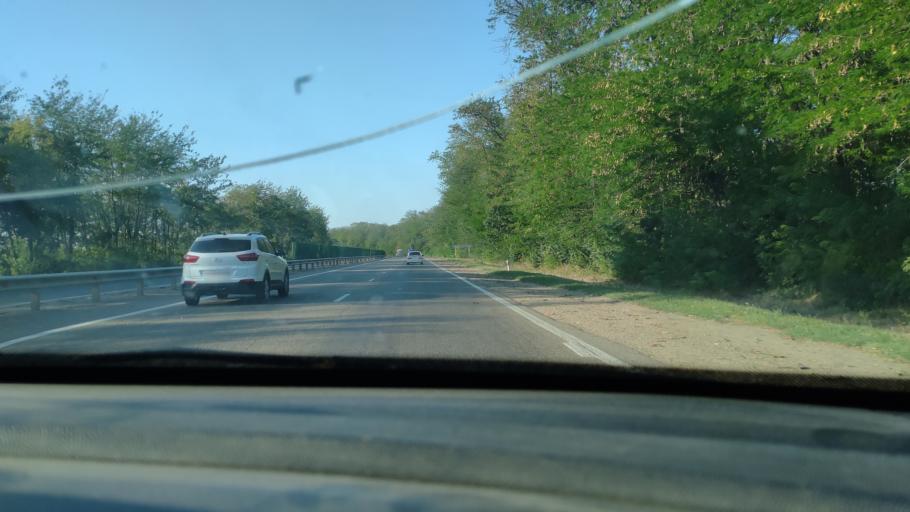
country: RU
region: Krasnodarskiy
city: Timashevsk
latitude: 45.5252
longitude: 38.9418
